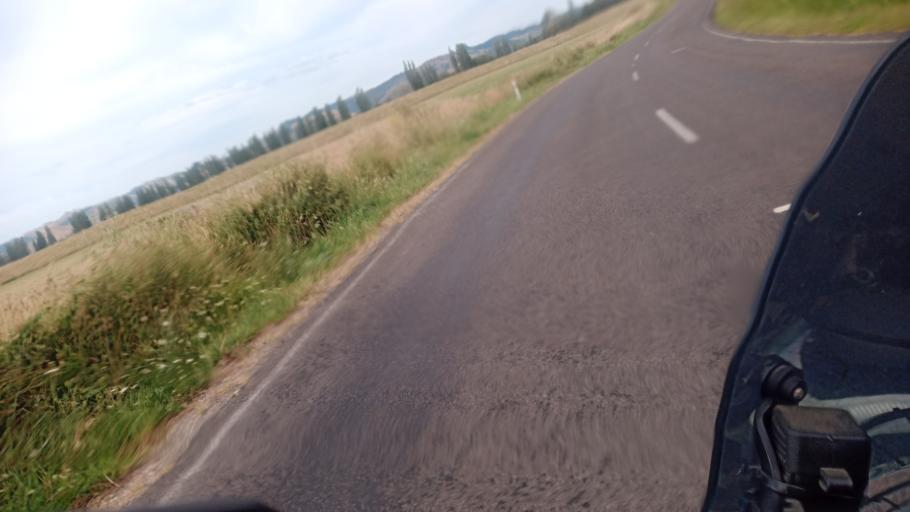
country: NZ
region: Gisborne
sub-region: Gisborne District
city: Gisborne
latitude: -38.5359
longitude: 177.8956
